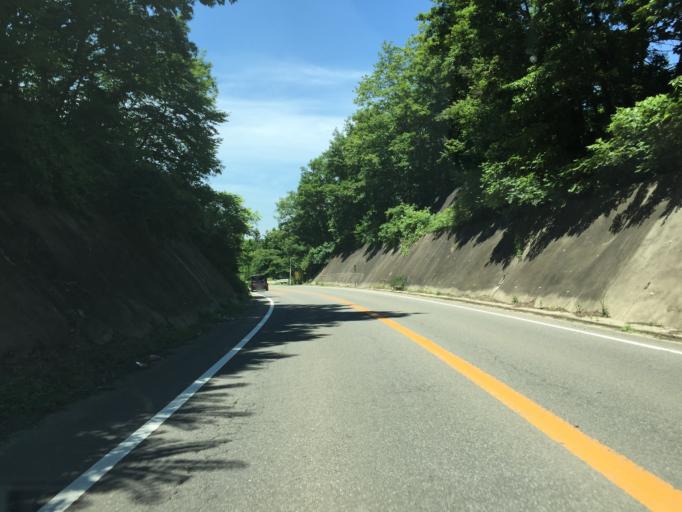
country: JP
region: Fukushima
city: Hobaramachi
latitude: 37.7780
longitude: 140.6028
